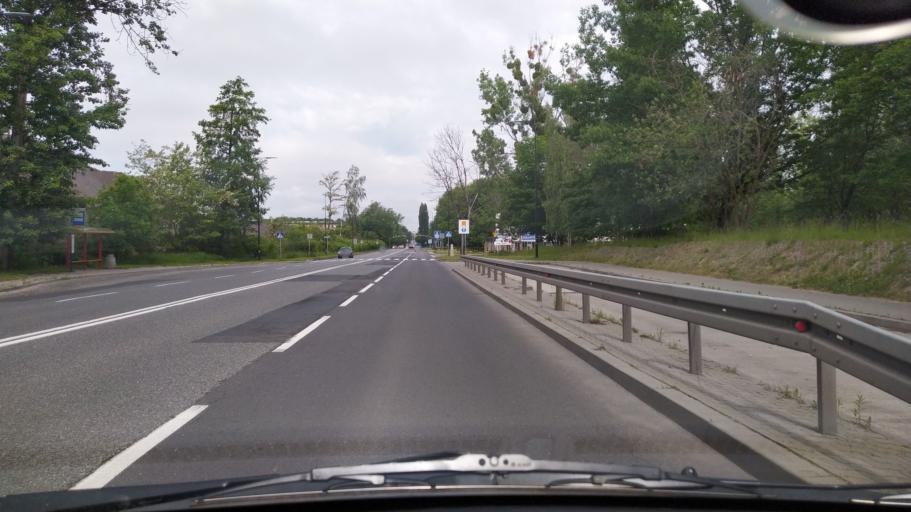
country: PL
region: Silesian Voivodeship
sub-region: Gliwice
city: Gliwice
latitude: 50.2780
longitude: 18.6932
